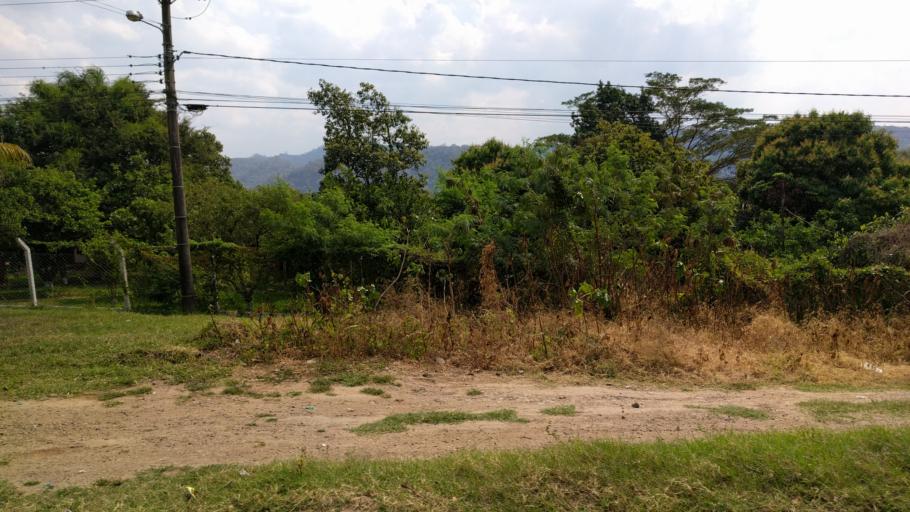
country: BO
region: Santa Cruz
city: Limoncito
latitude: -18.0231
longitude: -63.3997
